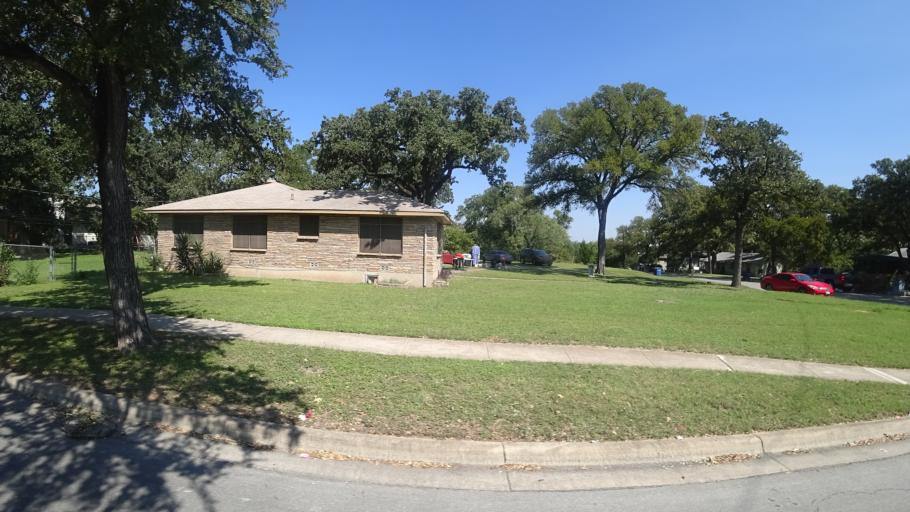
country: US
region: Texas
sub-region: Travis County
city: Austin
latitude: 30.3085
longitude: -97.6795
